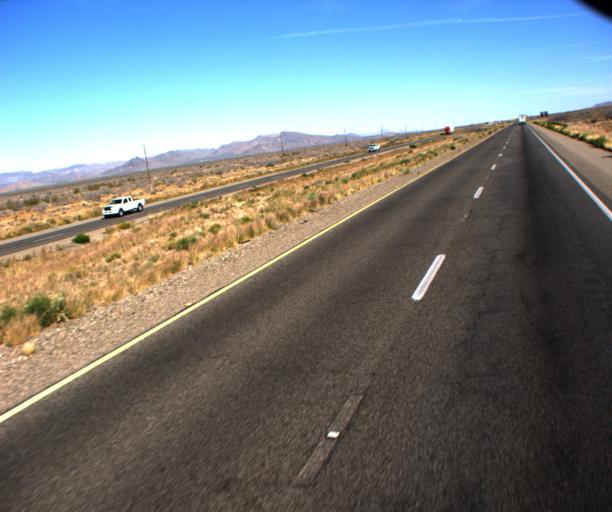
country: US
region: Arizona
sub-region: Mohave County
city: Golden Valley
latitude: 35.2776
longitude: -114.1727
